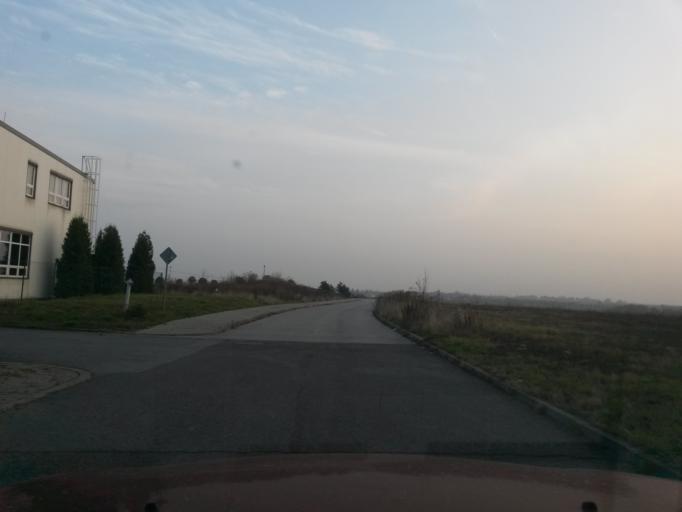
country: SK
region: Kosicky
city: Kosice
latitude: 48.6917
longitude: 21.2533
